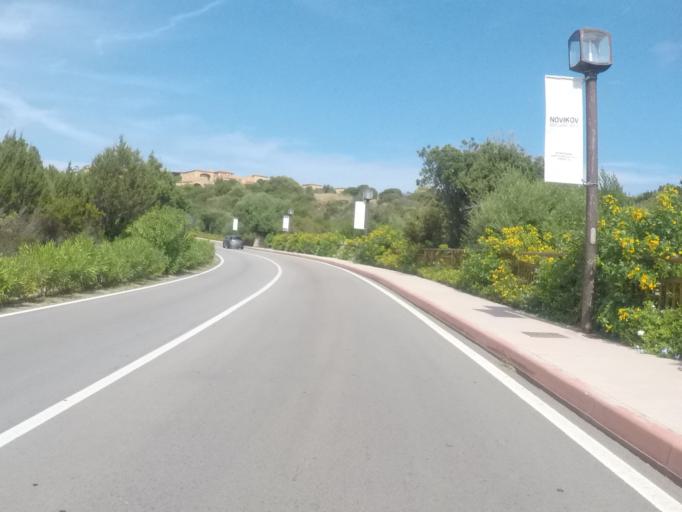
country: IT
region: Sardinia
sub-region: Provincia di Olbia-Tempio
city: Porto Cervo
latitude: 41.1239
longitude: 9.5366
